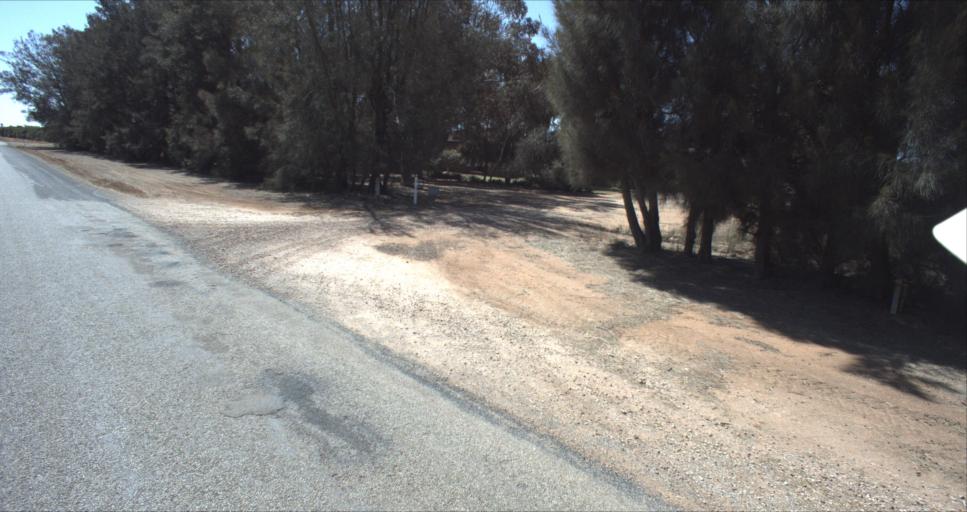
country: AU
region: New South Wales
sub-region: Leeton
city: Leeton
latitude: -34.5394
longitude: 146.3614
